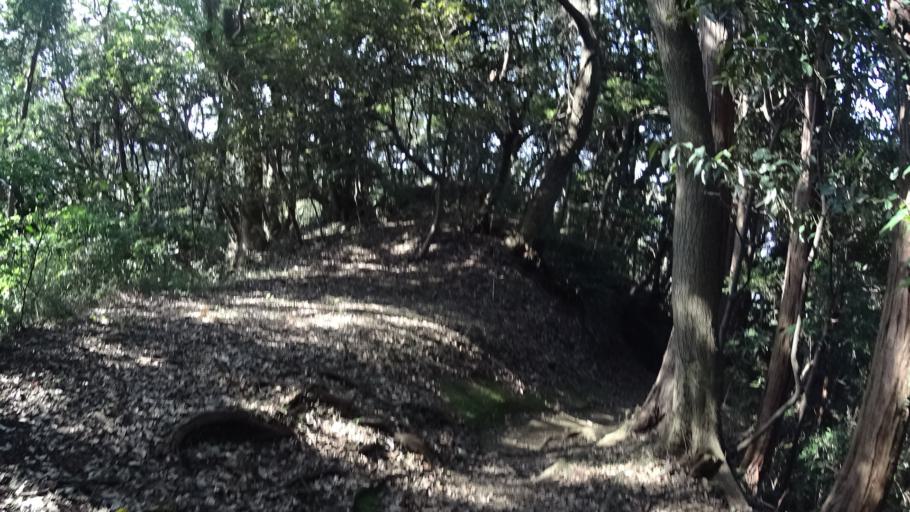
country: JP
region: Kanagawa
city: Zushi
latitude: 35.3573
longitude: 139.6028
